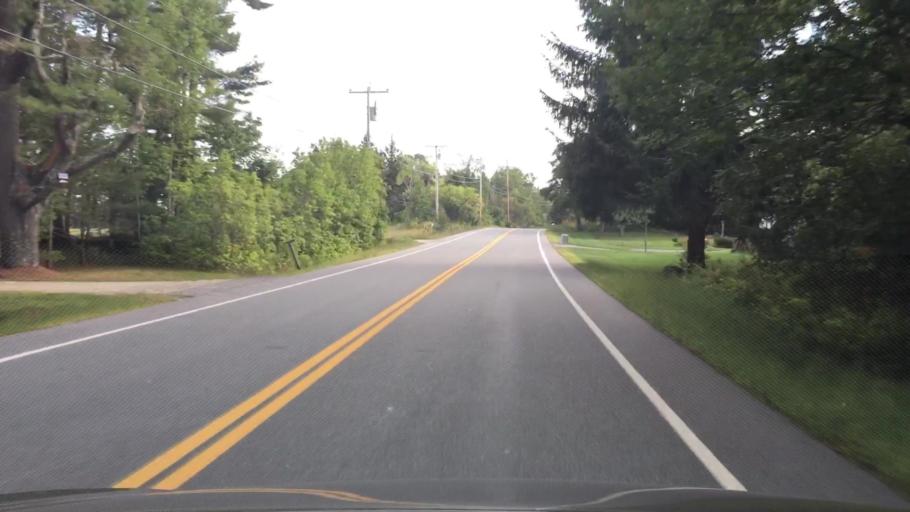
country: US
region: Maine
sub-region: Hancock County
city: Castine
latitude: 44.4438
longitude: -68.7869
